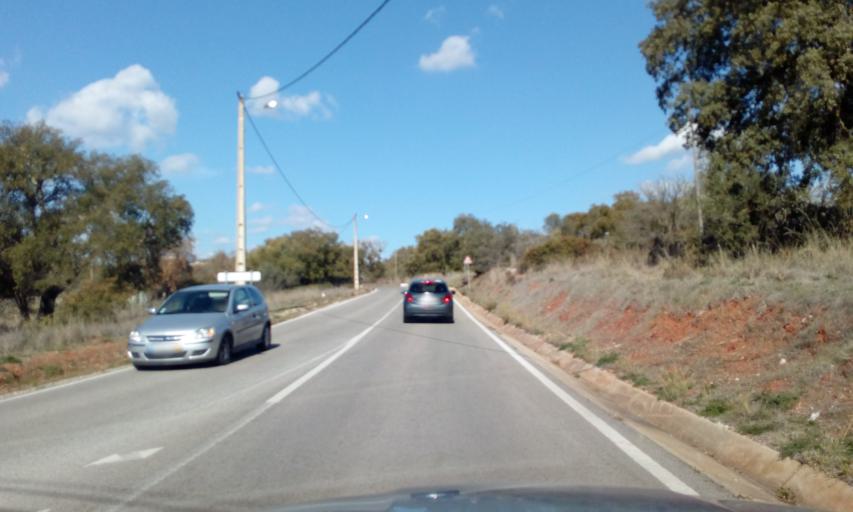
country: PT
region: Faro
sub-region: Loule
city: Loule
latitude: 37.2433
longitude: -8.0606
